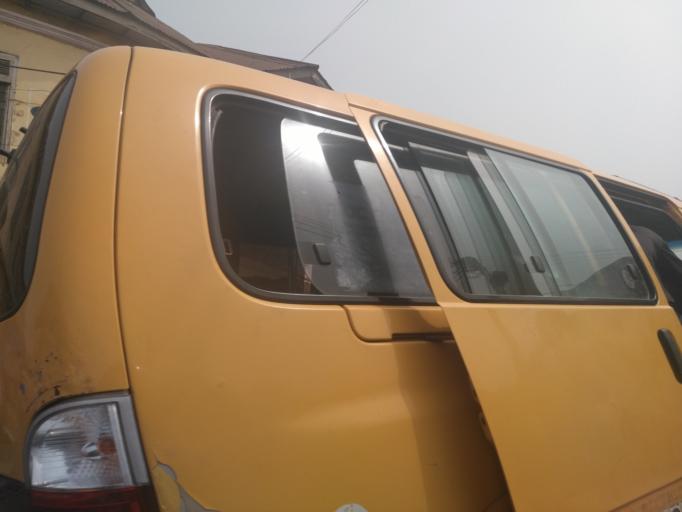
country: GH
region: Ashanti
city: Kumasi
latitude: 6.7025
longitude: -1.6218
